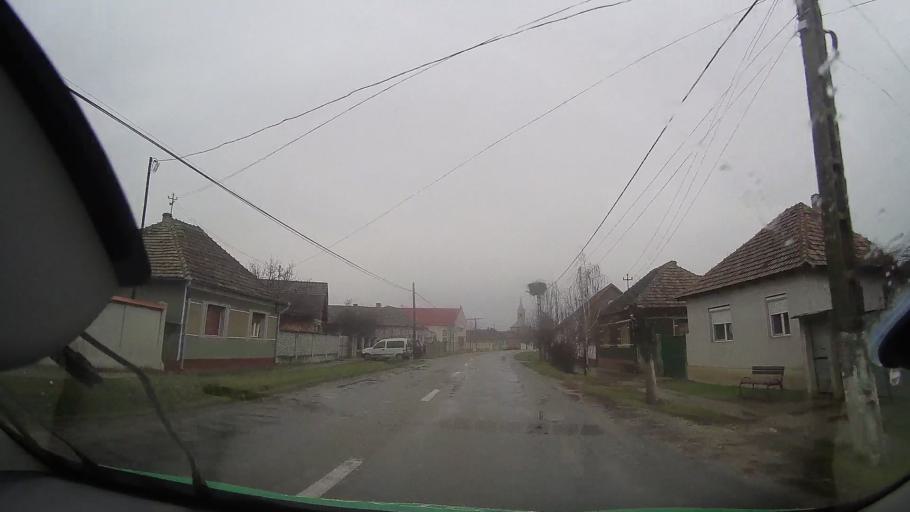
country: RO
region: Bihor
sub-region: Comuna Tinca
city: Gurbediu
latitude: 46.7905
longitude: 21.8656
